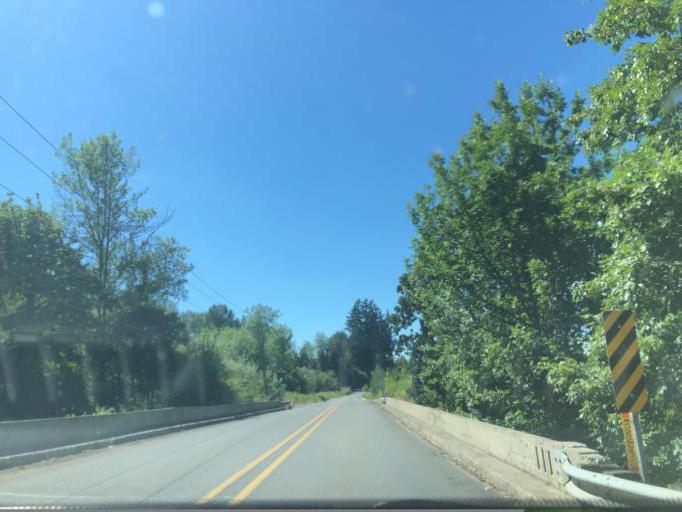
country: US
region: Oregon
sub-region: Marion County
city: Hubbard
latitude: 45.1737
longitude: -122.7371
